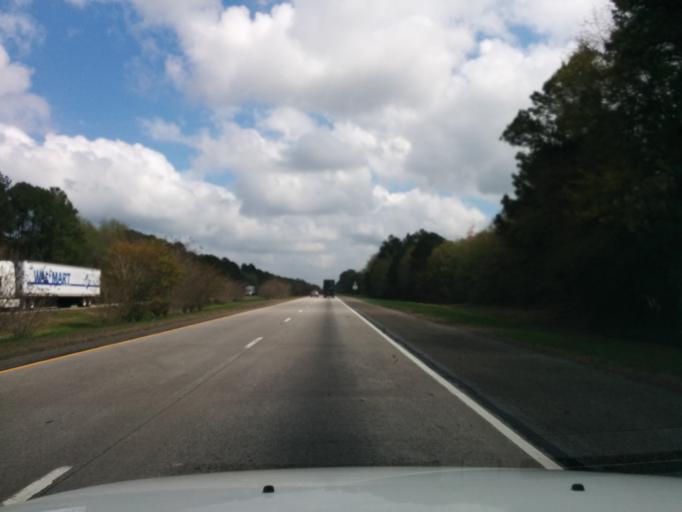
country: US
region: Georgia
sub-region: Bryan County
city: Pembroke
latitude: 32.2306
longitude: -81.6375
